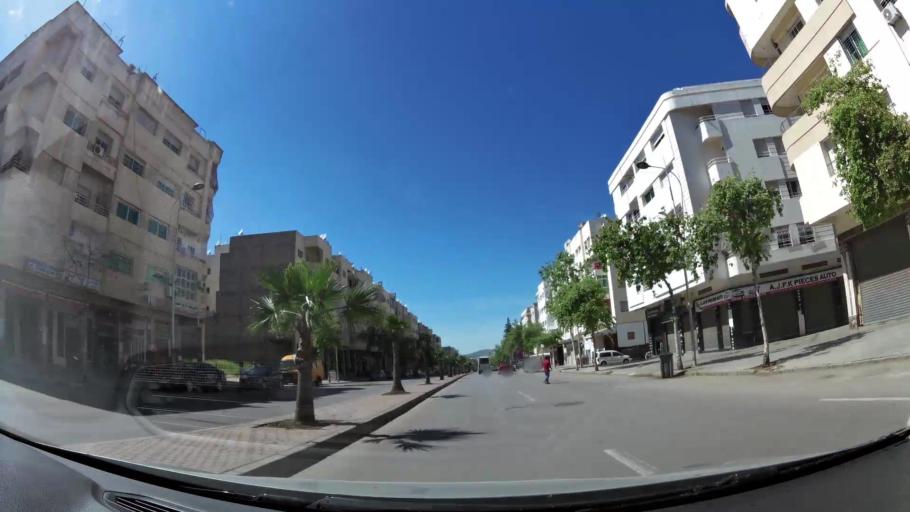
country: MA
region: Fes-Boulemane
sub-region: Fes
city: Fes
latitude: 34.0211
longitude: -4.9877
